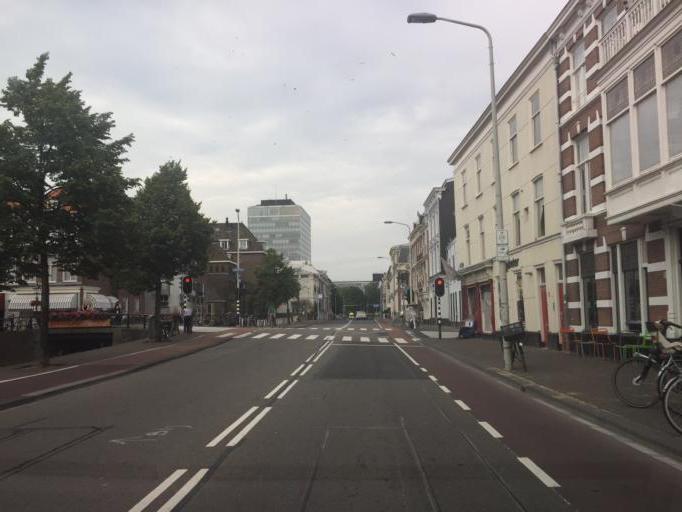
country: NL
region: South Holland
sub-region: Gemeente Den Haag
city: The Hague
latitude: 52.0862
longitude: 4.3109
